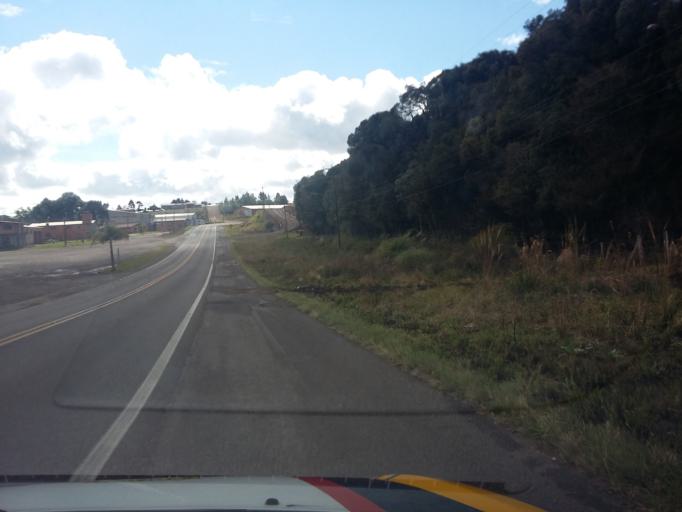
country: BR
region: Rio Grande do Sul
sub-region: Sao Marcos
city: Sao Marcos
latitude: -28.7821
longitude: -51.0972
